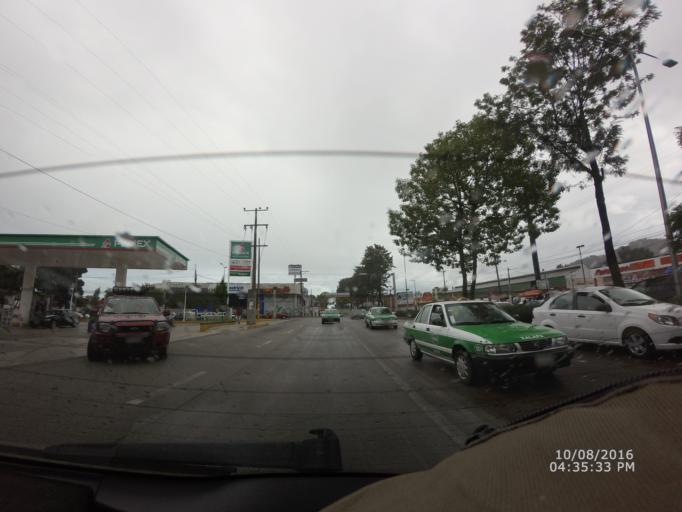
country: MX
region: Veracruz
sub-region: Xalapa
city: Xalapa de Enriquez
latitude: 19.5603
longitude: -96.9230
